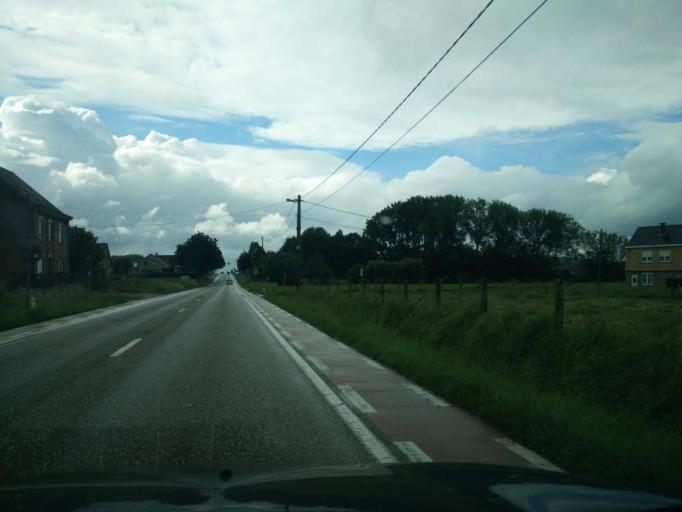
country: BE
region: Flanders
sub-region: Provincie Vlaams-Brabant
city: Gooik
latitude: 50.7905
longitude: 4.0763
